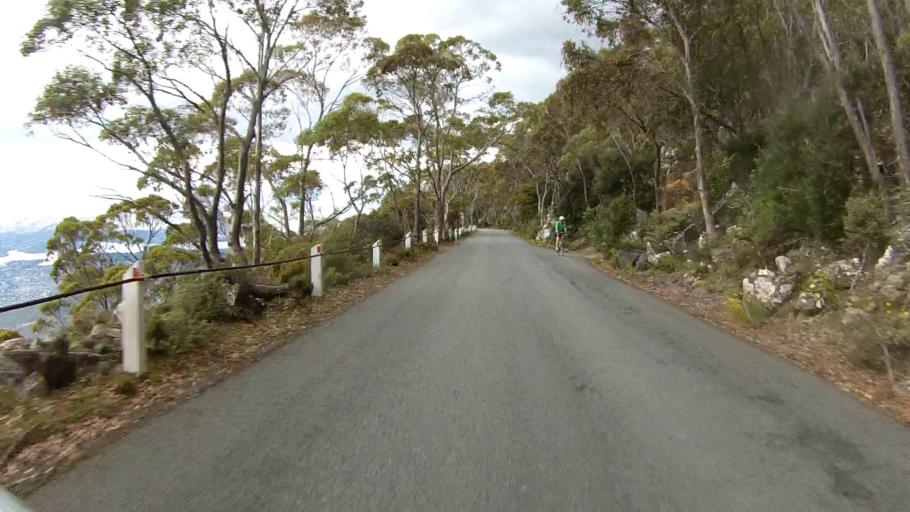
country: AU
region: Tasmania
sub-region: Glenorchy
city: West Moonah
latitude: -42.8890
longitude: 147.2314
